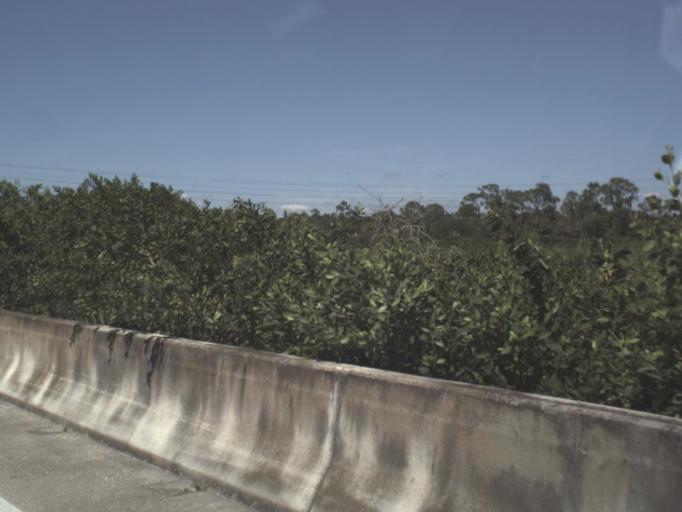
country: US
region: Florida
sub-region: Lee County
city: Tice
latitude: 26.7085
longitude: -81.8063
